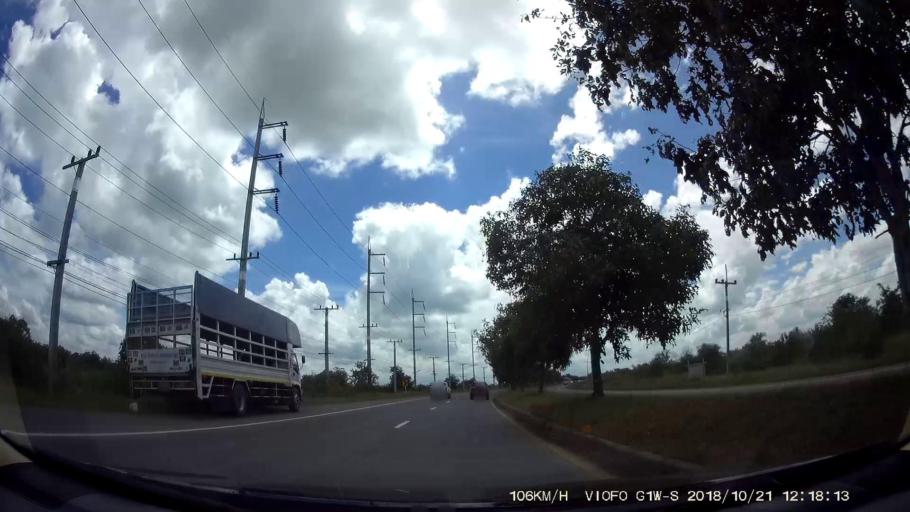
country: TH
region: Nakhon Ratchasima
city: Dan Khun Thot
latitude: 15.3196
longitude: 101.8181
